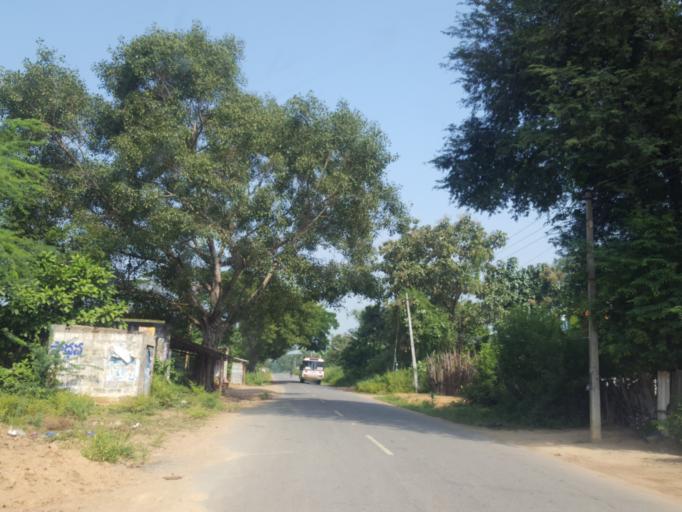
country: IN
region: Telangana
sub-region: Khammam
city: Yellandu
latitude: 17.6138
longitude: 80.3108
